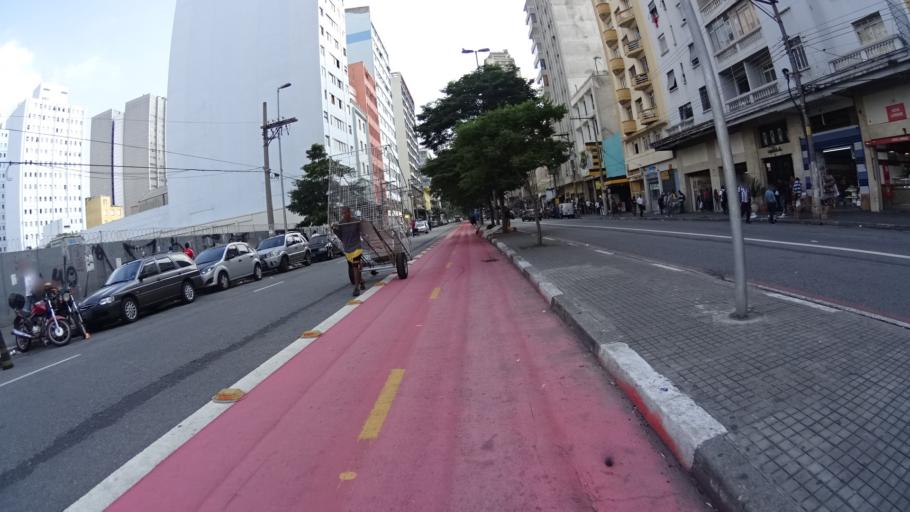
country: BR
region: Sao Paulo
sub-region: Sao Paulo
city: Sao Paulo
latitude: -23.5363
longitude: -46.6356
